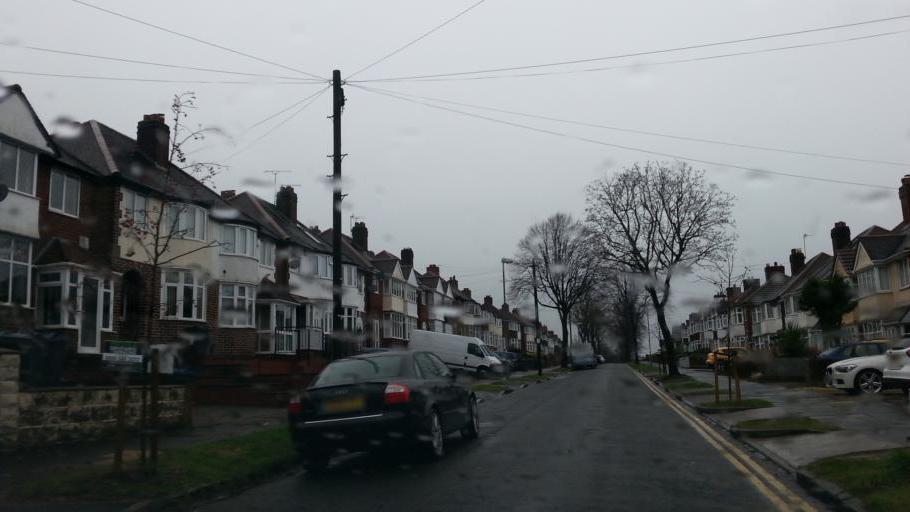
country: GB
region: England
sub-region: City and Borough of Birmingham
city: Hockley
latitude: 52.5400
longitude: -1.9231
